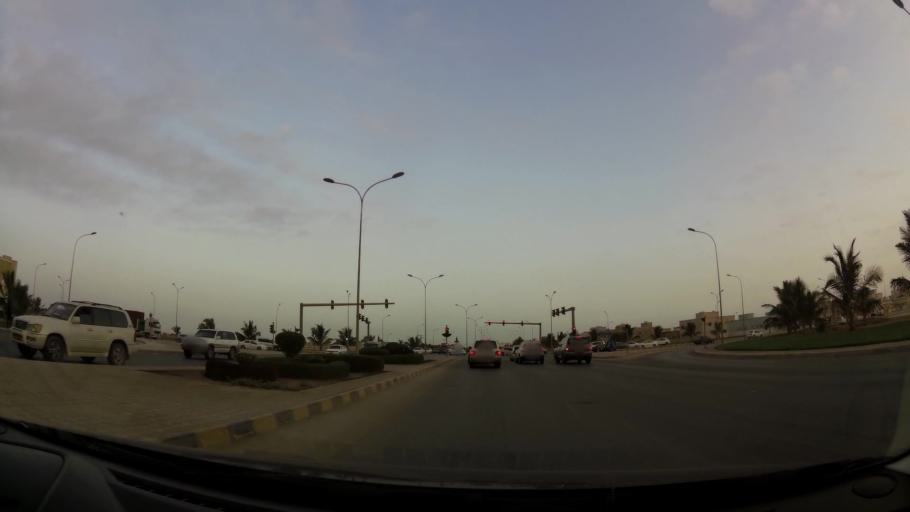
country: OM
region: Zufar
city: Salalah
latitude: 17.0211
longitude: 54.0339
